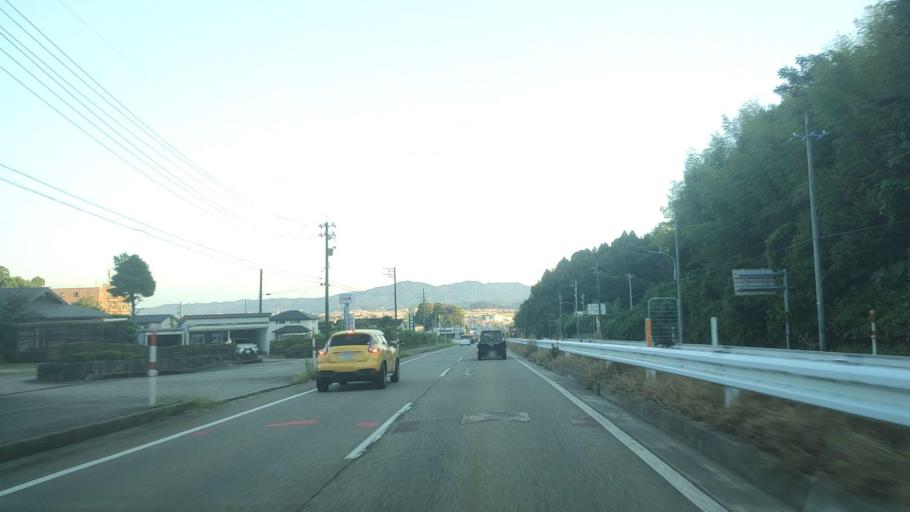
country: JP
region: Toyama
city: Himi
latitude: 36.8493
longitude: 136.9792
